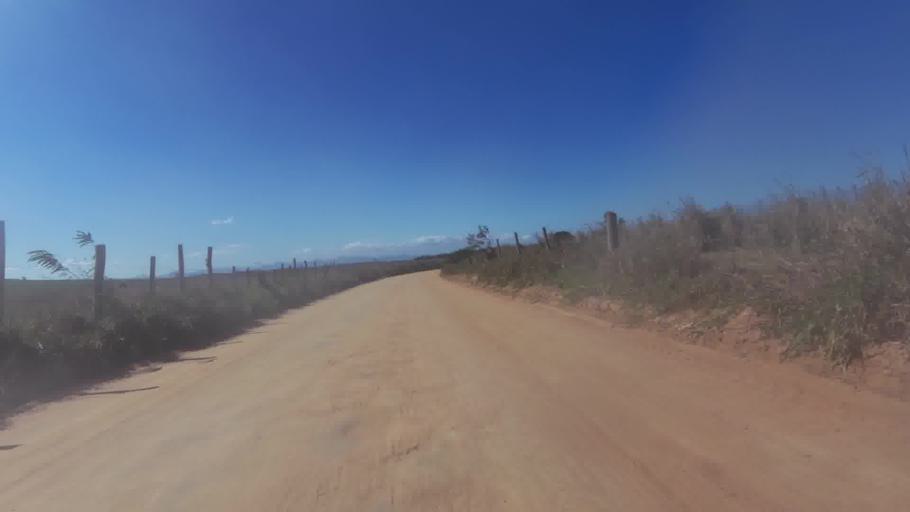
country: BR
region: Espirito Santo
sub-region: Marataizes
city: Marataizes
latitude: -21.1371
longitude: -40.9929
